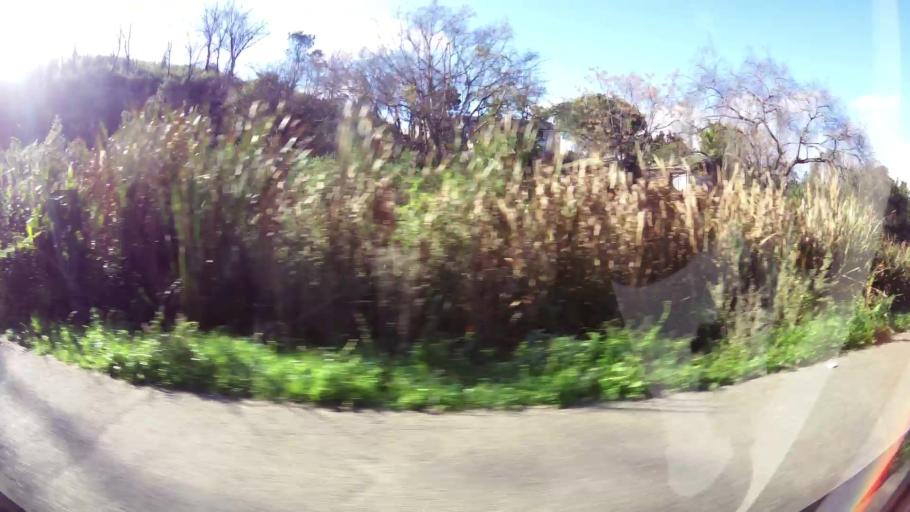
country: ZA
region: Western Cape
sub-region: Eden District Municipality
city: Knysna
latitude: -34.0321
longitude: 23.0469
